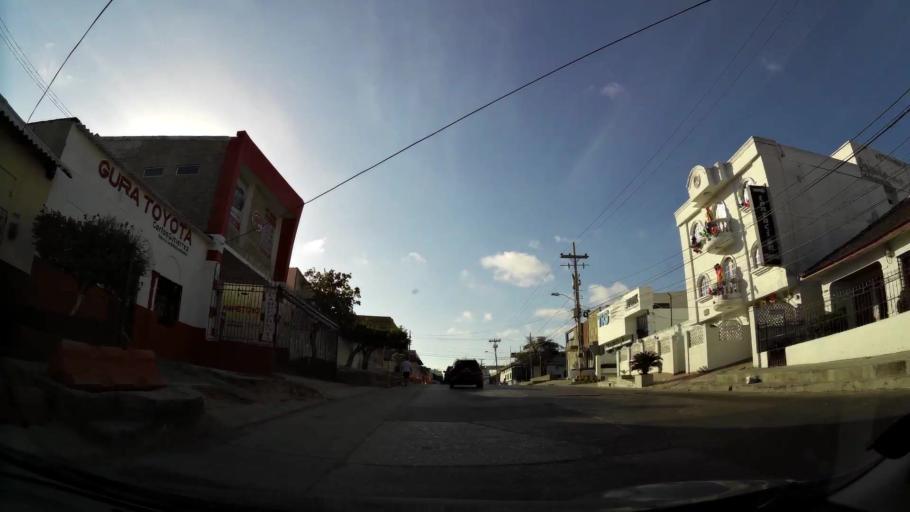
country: CO
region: Atlantico
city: Barranquilla
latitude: 10.9851
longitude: -74.7943
